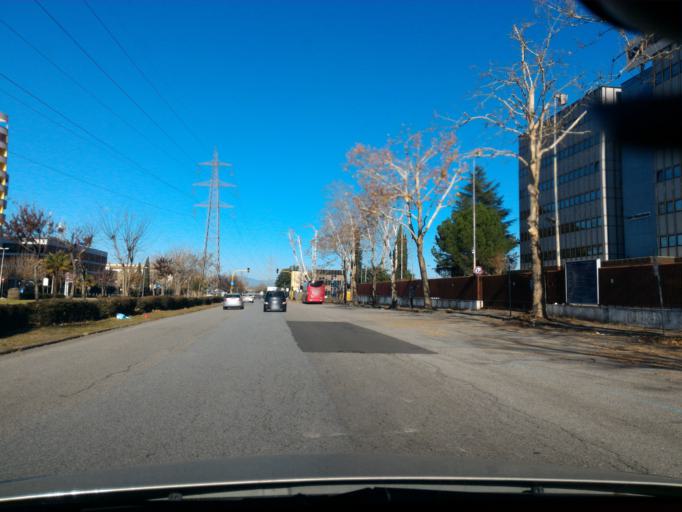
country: IT
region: Calabria
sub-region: Provincia di Cosenza
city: Cosenza
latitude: 39.3210
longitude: 16.2570
